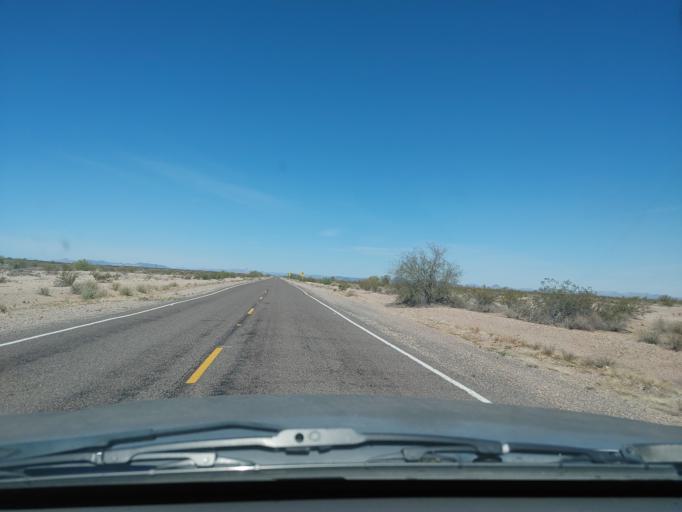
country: US
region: Arizona
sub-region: Maricopa County
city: Gila Bend
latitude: 32.8885
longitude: -113.2377
